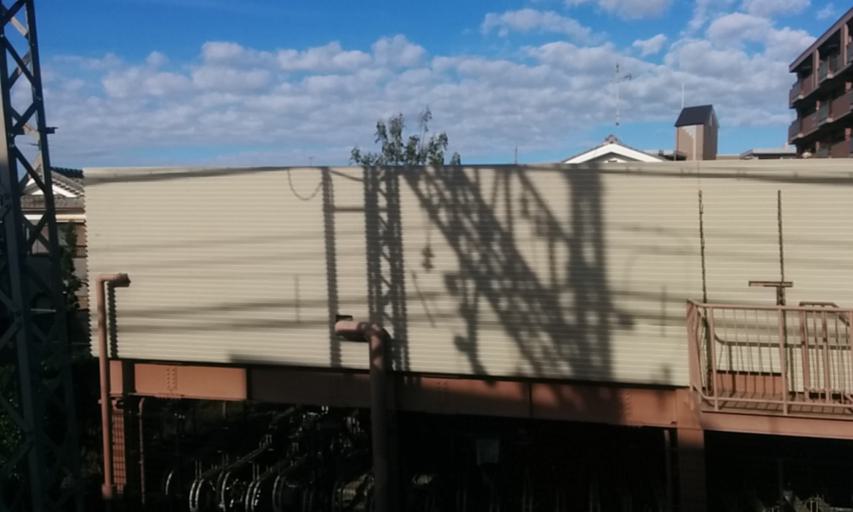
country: JP
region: Kyoto
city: Uji
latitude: 34.8839
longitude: 135.7793
